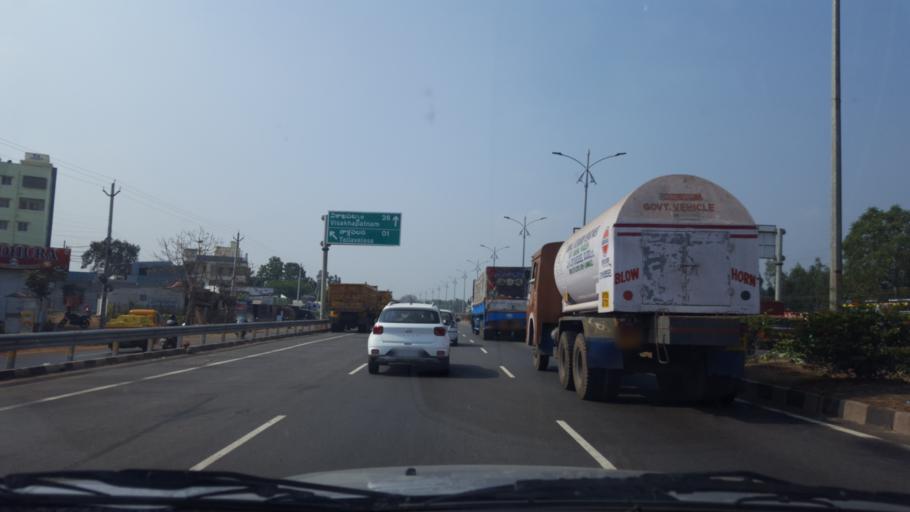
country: IN
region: Andhra Pradesh
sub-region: Vishakhapatnam
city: Bhimunipatnam
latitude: 17.9201
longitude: 83.4172
